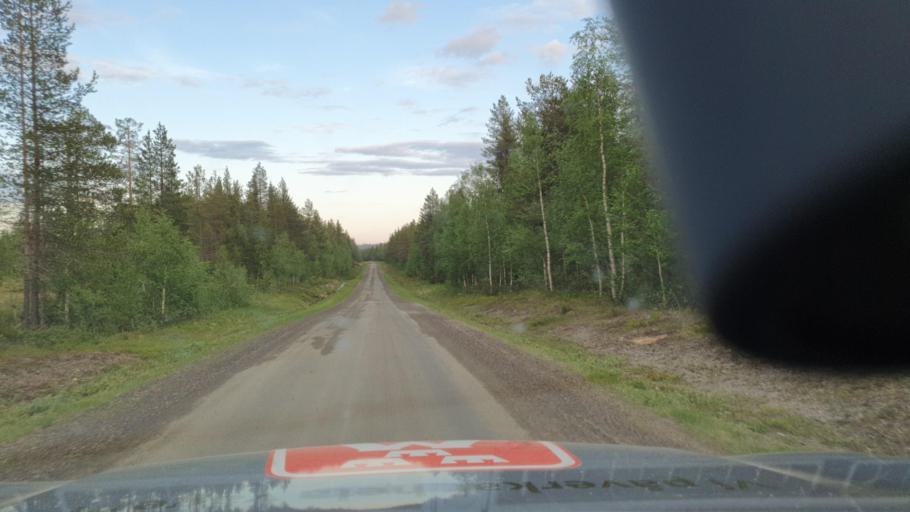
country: SE
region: Norrbotten
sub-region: Bodens Kommun
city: Boden
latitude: 66.5869
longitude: 21.3905
